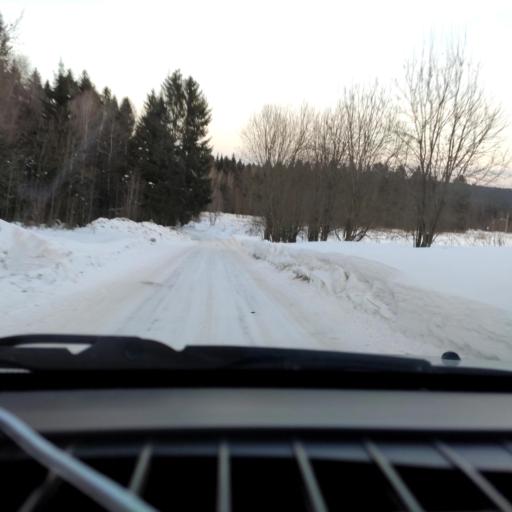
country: RU
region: Perm
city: Ferma
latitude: 57.9658
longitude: 56.3829
